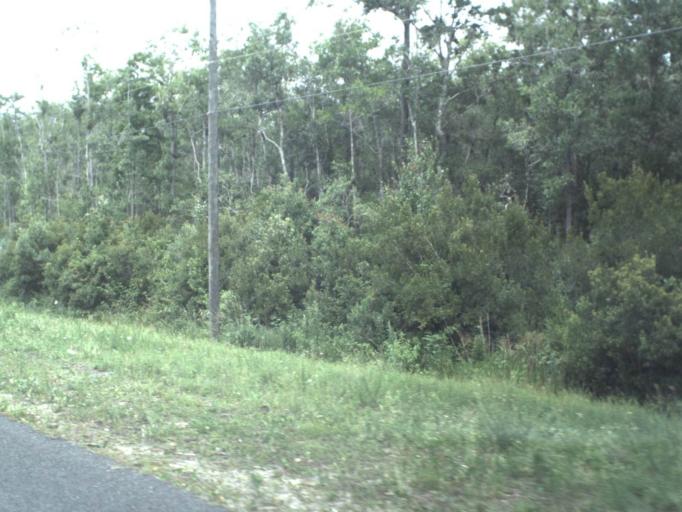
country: US
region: Florida
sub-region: Nassau County
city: Callahan
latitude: 30.6074
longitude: -81.7439
